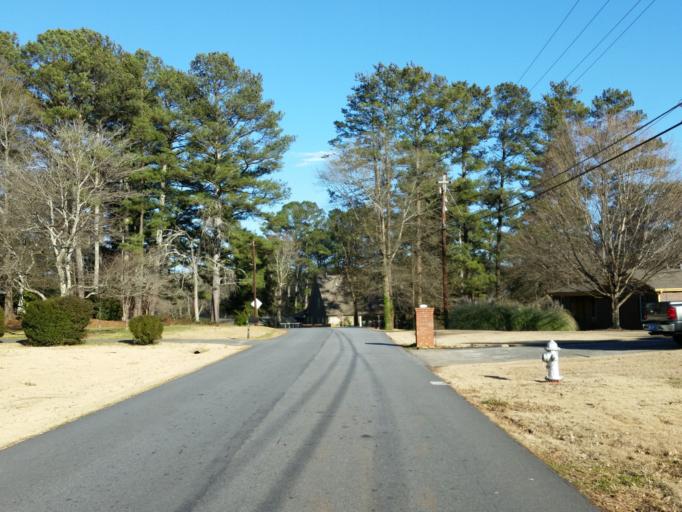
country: US
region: Georgia
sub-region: Cherokee County
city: Woodstock
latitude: 34.0301
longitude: -84.5218
